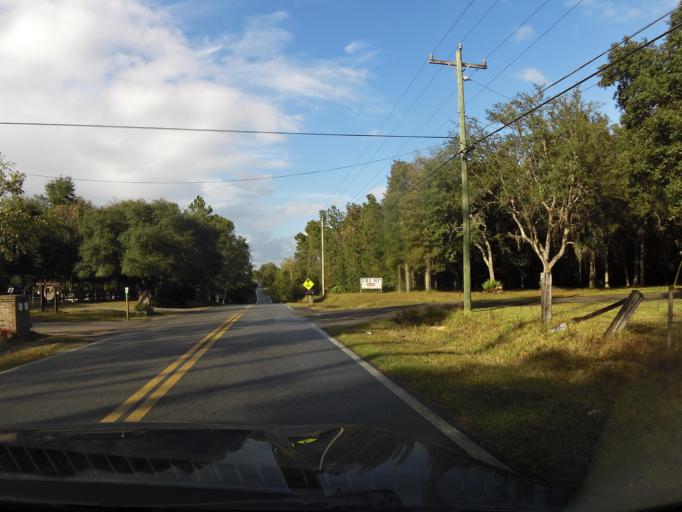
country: US
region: Florida
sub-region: Clay County
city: Asbury Lake
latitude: 30.0153
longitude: -81.8465
